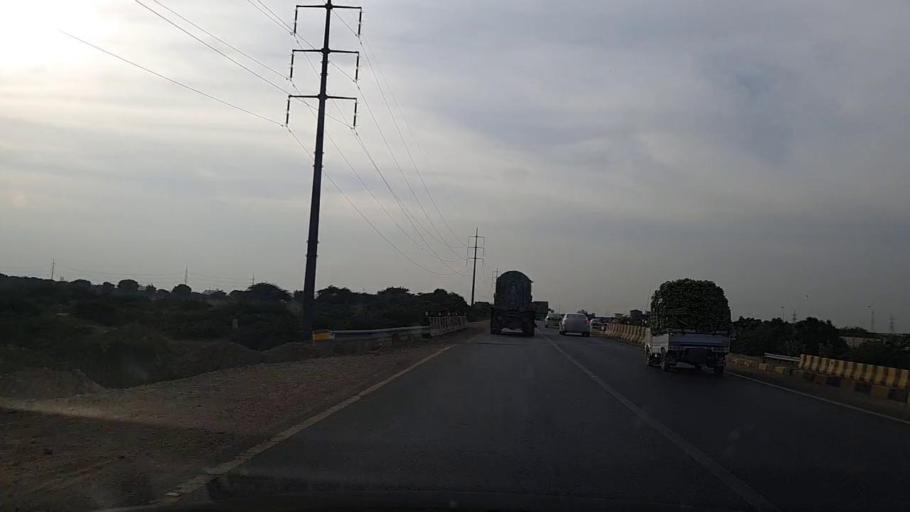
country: PK
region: Sindh
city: Gharo
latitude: 24.8373
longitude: 67.4495
